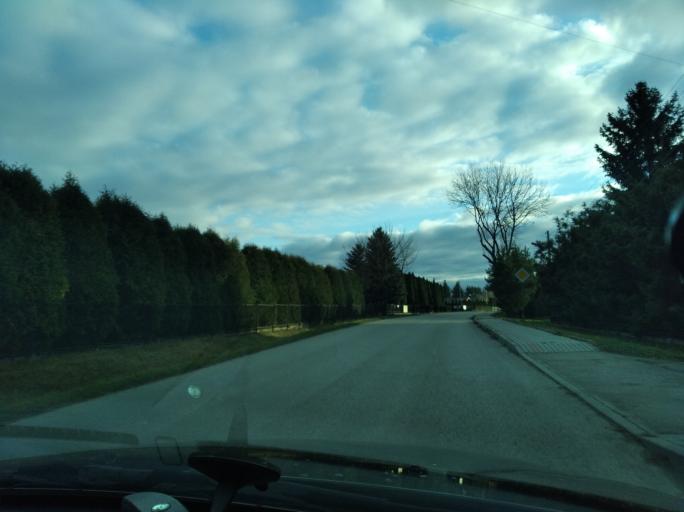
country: PL
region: Subcarpathian Voivodeship
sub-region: Powiat rzeszowski
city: Krasne
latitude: 50.0595
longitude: 22.1195
